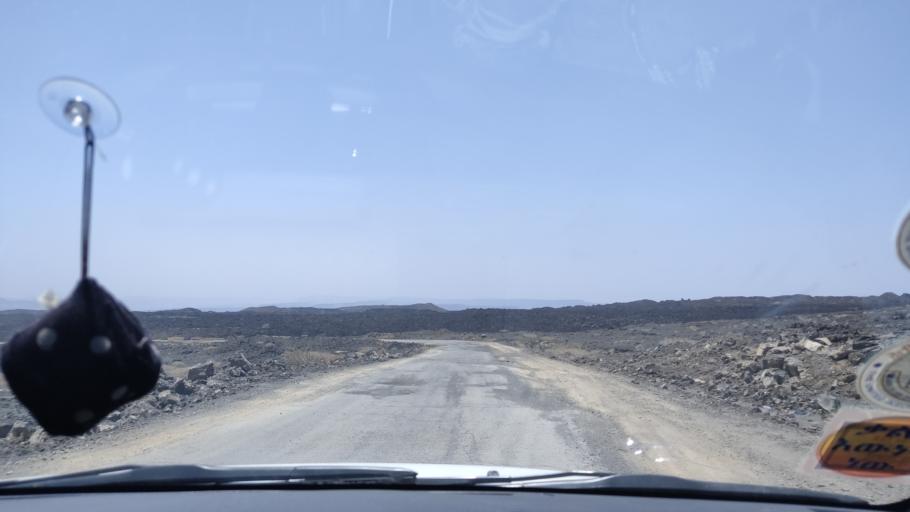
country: DJ
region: Tadjourah
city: Dorra
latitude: 12.3965
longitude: 42.1757
